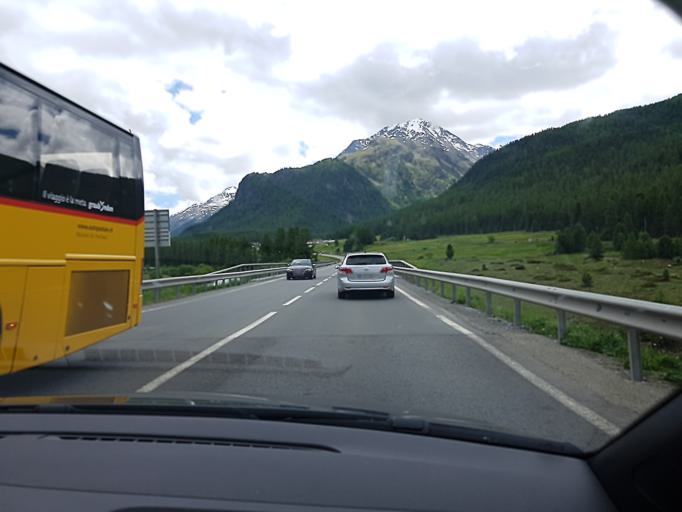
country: CH
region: Grisons
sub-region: Maloja District
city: Pontresina
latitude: 46.5028
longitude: 9.8877
